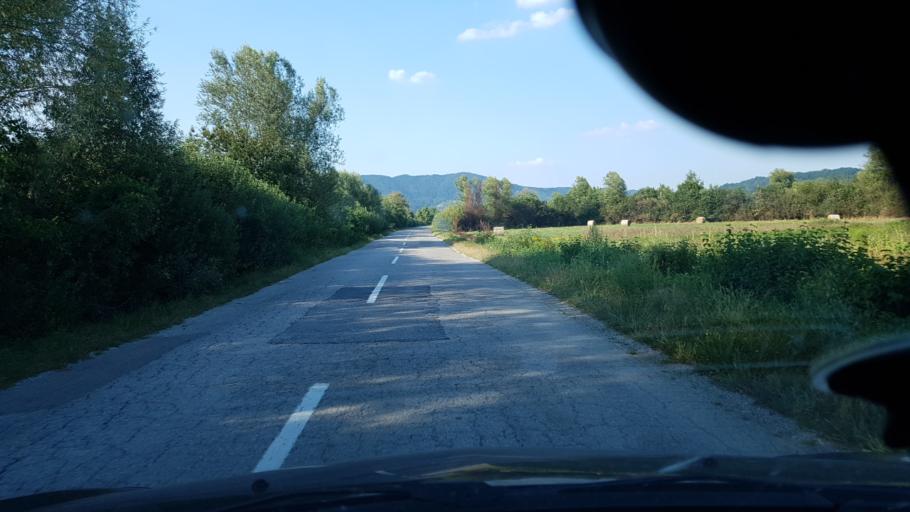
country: SI
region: Bistrica ob Sotli
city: Bistrica ob Sotli
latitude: 46.0130
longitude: 15.7163
